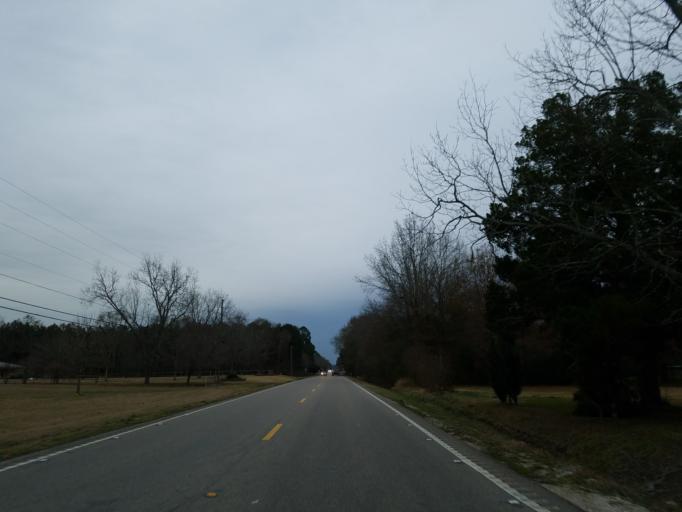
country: US
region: Mississippi
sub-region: Forrest County
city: Glendale
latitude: 31.4908
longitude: -89.2810
